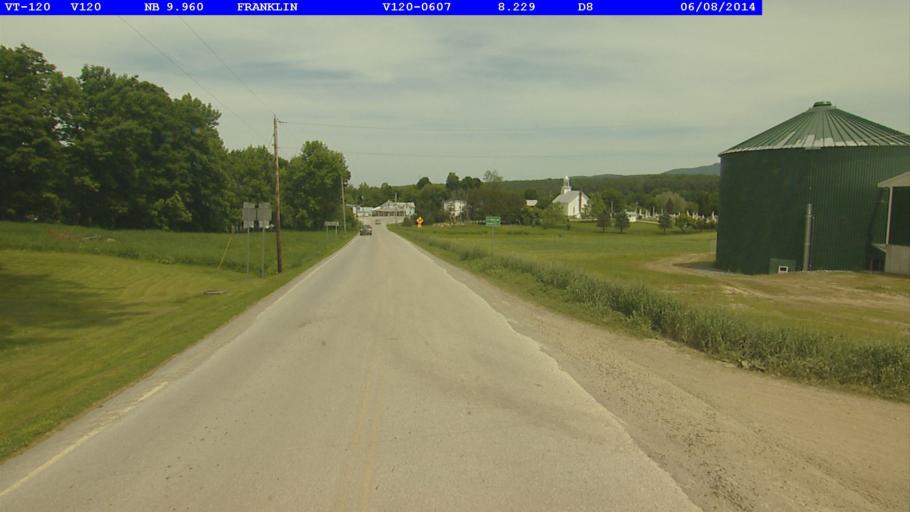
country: US
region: Vermont
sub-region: Franklin County
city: Enosburg Falls
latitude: 44.9942
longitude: -72.8327
